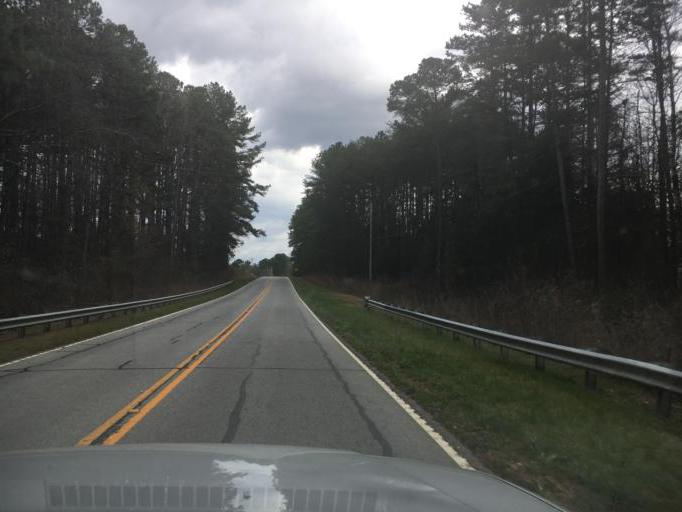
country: US
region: South Carolina
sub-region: Oconee County
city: Westminster
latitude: 34.7096
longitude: -83.0716
